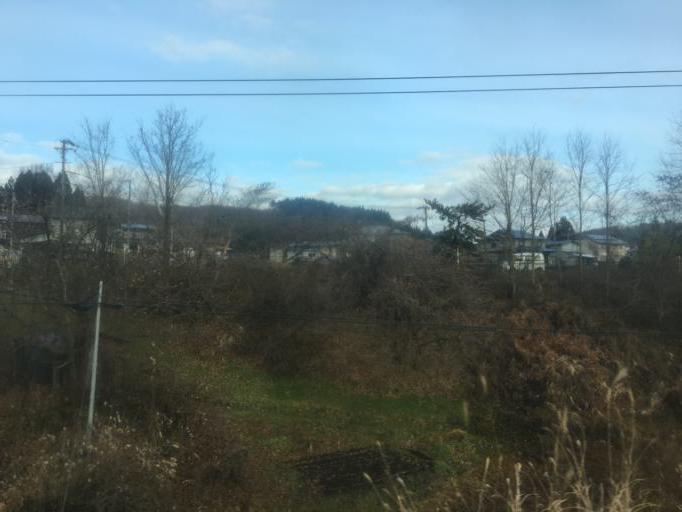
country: JP
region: Akita
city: Takanosu
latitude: 40.2639
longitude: 140.4196
